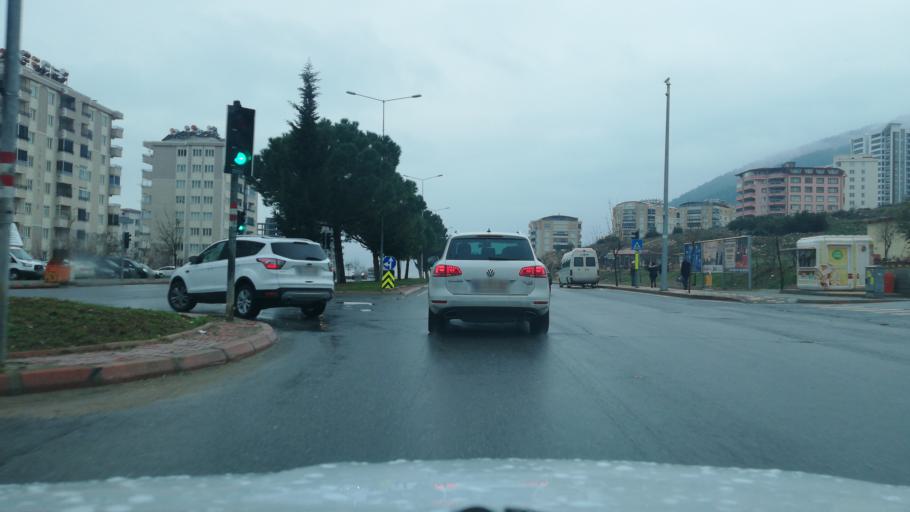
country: TR
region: Kahramanmaras
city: Kahramanmaras
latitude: 37.5957
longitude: 36.8515
